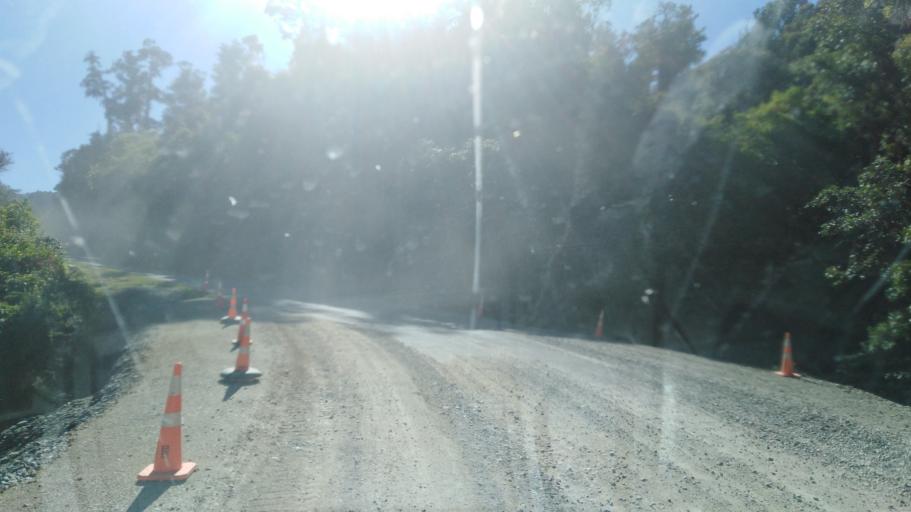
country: NZ
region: West Coast
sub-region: Buller District
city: Westport
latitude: -41.5273
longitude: 172.0003
